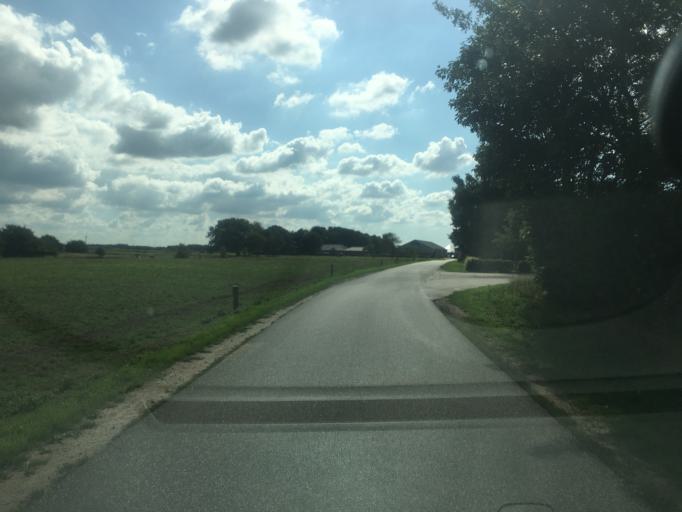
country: DK
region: South Denmark
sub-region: Tonder Kommune
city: Logumkloster
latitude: 55.0000
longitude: 9.0151
